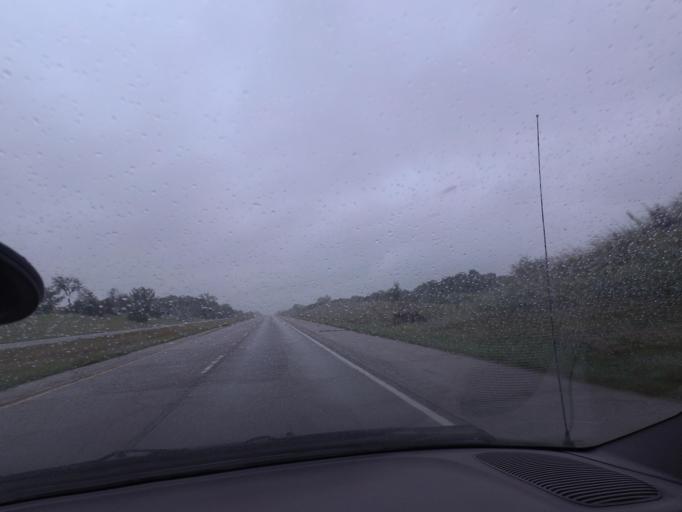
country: US
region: Illinois
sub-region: Pike County
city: Barry
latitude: 39.6895
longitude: -90.9158
